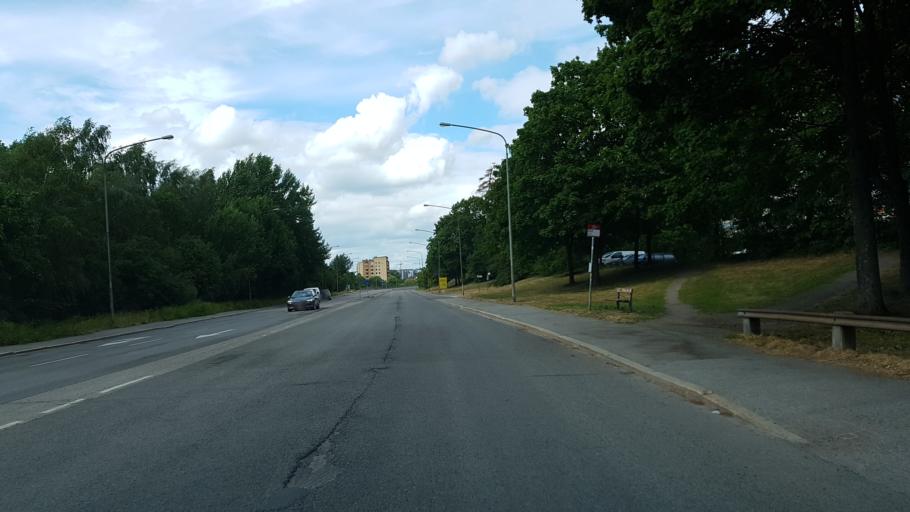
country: SE
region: Stockholm
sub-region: Solna Kommun
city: Solna
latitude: 59.3507
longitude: 17.9897
